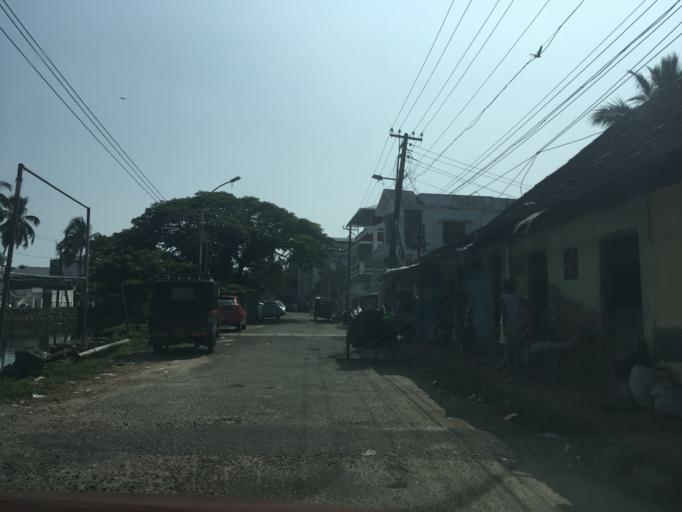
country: IN
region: Kerala
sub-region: Ernakulam
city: Cochin
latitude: 9.9656
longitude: 76.2496
